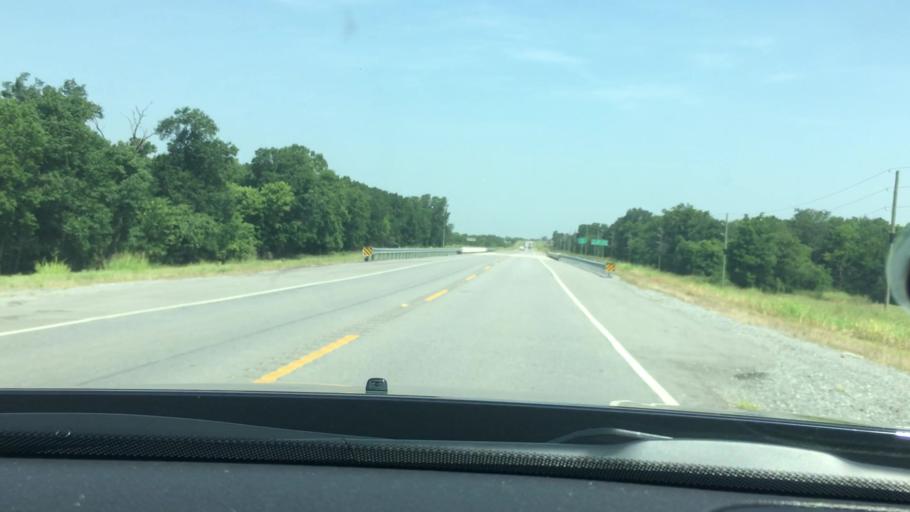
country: US
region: Oklahoma
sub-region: Coal County
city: Coalgate
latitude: 34.4443
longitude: -96.2059
